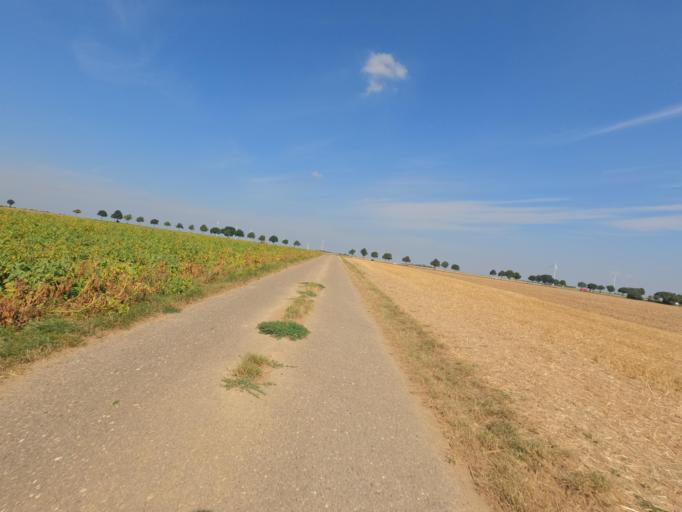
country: DE
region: North Rhine-Westphalia
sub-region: Regierungsbezirk Koln
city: Linnich
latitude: 50.9893
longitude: 6.3337
